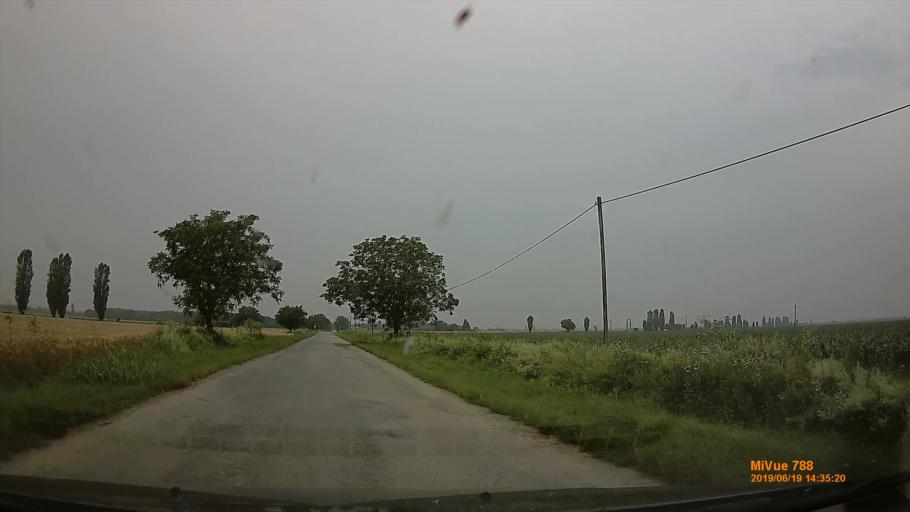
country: HU
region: Baranya
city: Szigetvar
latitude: 46.0726
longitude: 17.7680
